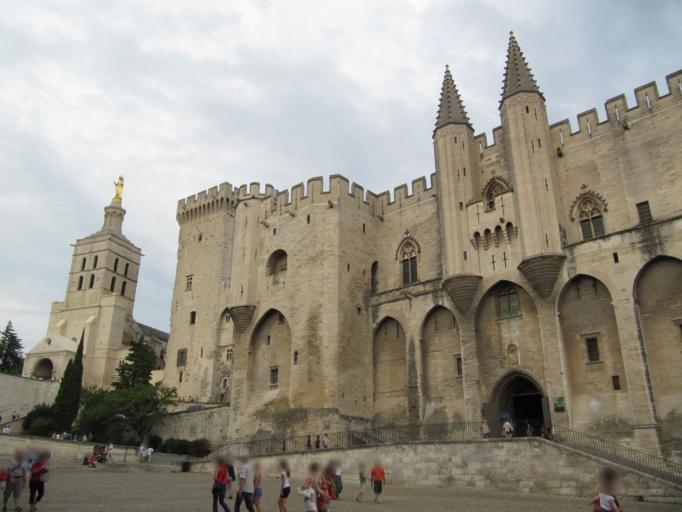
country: FR
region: Provence-Alpes-Cote d'Azur
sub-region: Departement du Vaucluse
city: Avignon
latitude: 43.9506
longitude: 4.8064
